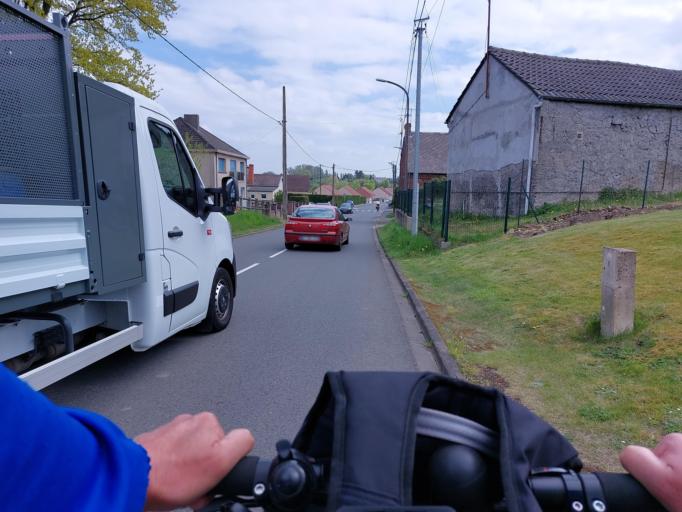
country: FR
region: Nord-Pas-de-Calais
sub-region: Departement du Nord
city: Hautmont
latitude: 50.2675
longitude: 3.8957
